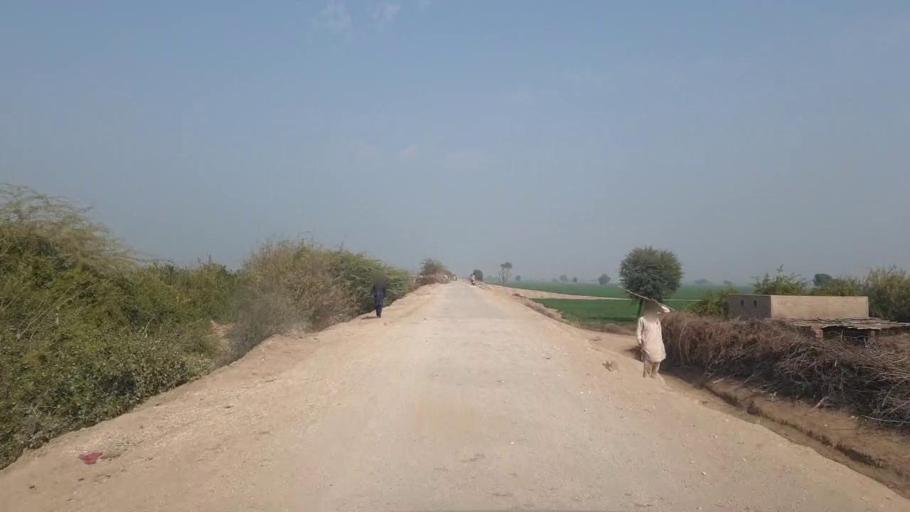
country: PK
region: Sindh
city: Hala
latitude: 25.7726
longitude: 68.3929
